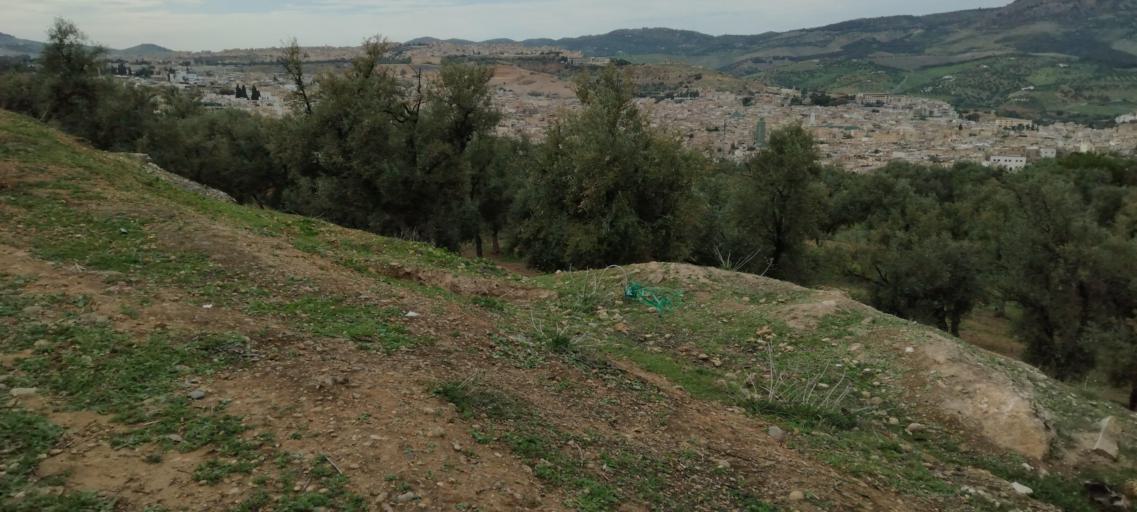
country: MA
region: Fes-Boulemane
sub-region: Fes
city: Fes
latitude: 34.0541
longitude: -4.9689
